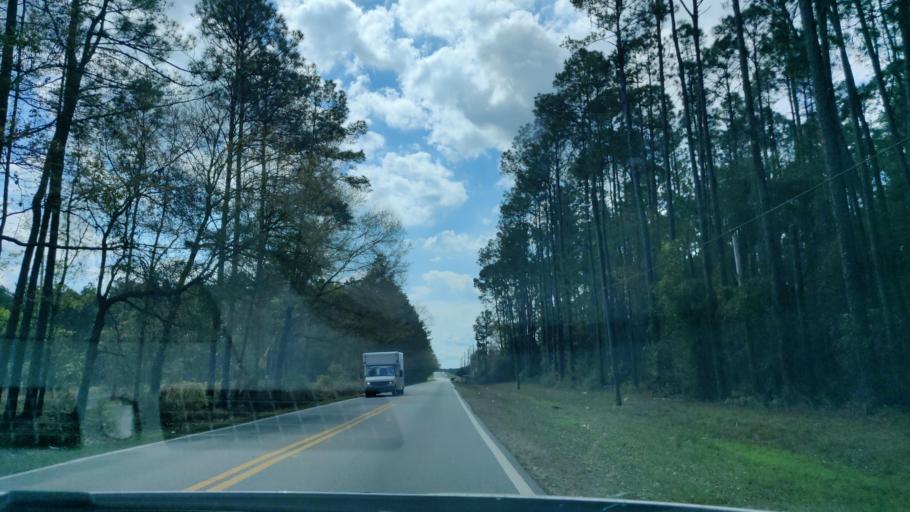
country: US
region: Florida
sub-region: Duval County
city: Baldwin
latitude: 30.2972
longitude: -81.9664
